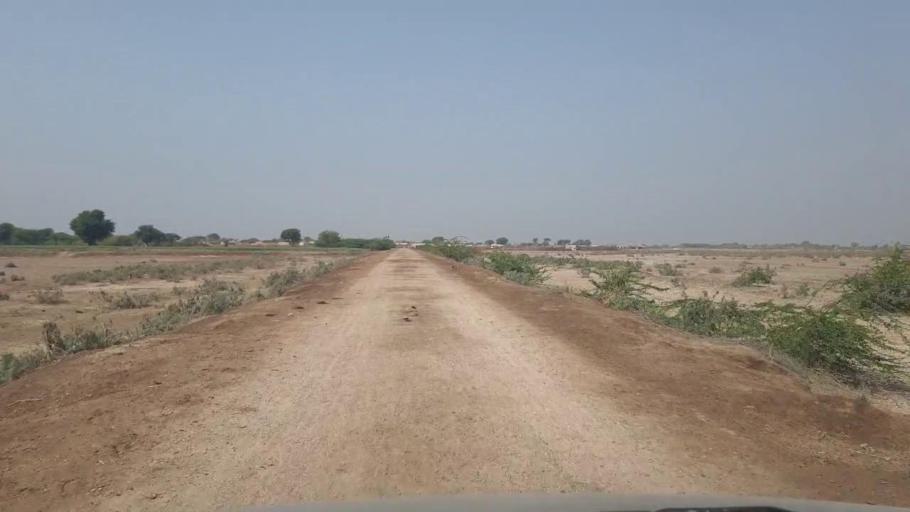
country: PK
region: Sindh
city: Chor
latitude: 25.4651
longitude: 69.7411
